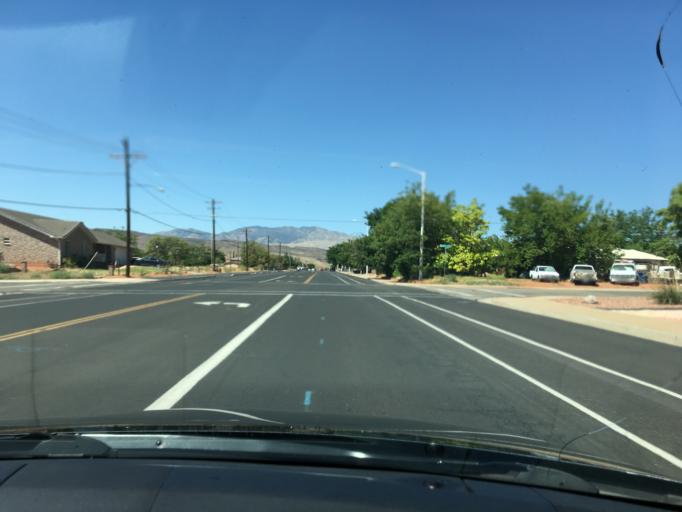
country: US
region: Utah
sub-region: Washington County
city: Ivins
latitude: 37.1684
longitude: -113.6769
